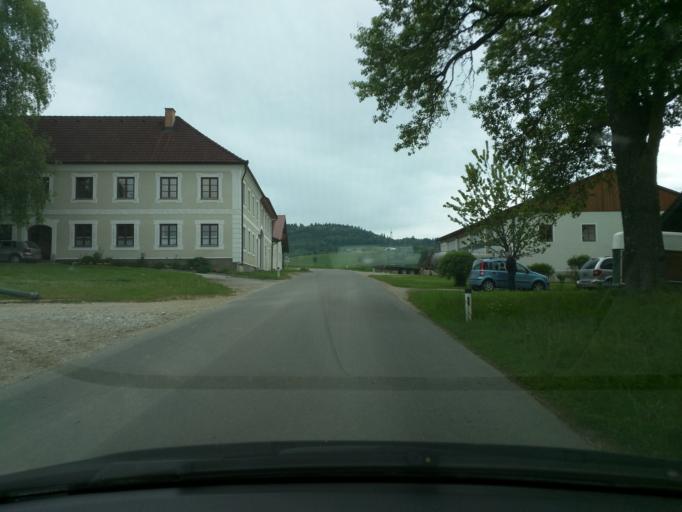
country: AT
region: Lower Austria
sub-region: Politischer Bezirk Melk
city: Blindenmarkt
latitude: 48.1405
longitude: 14.9739
